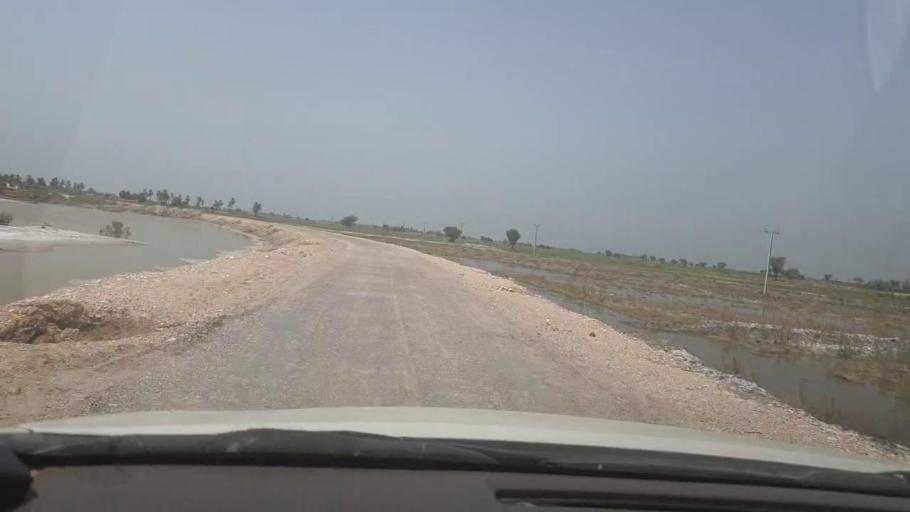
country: PK
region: Sindh
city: Garhi Yasin
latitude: 27.9759
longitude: 68.5475
